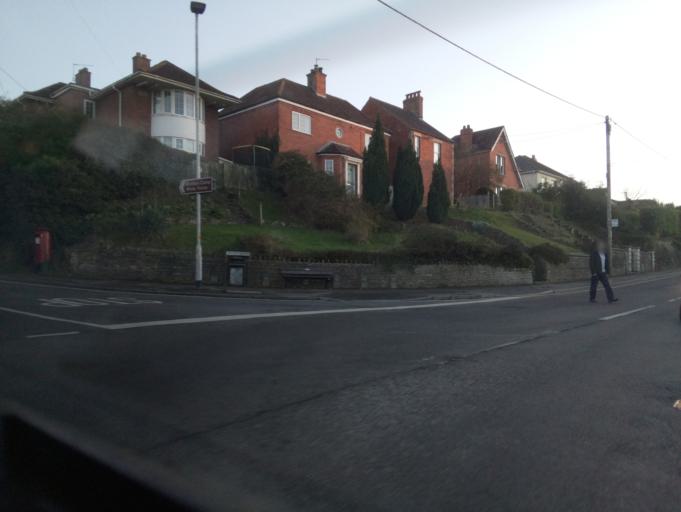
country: GB
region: England
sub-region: Wiltshire
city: Westbury
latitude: 51.2614
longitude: -2.1779
